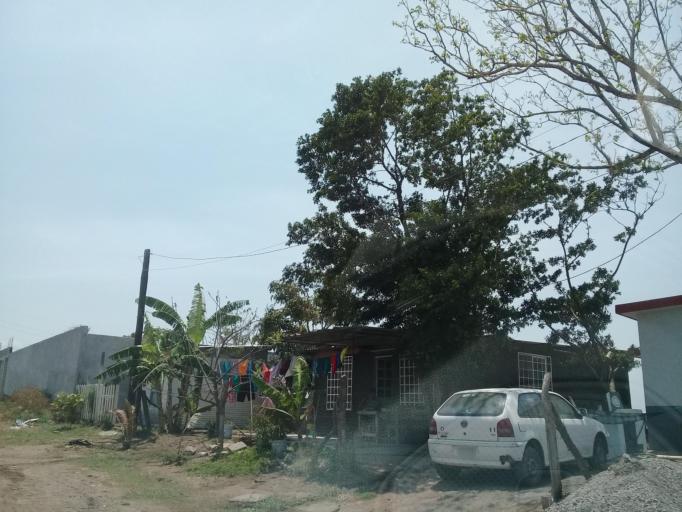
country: MX
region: Veracruz
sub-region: Veracruz
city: Las Amapolas
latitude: 19.1593
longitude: -96.2149
